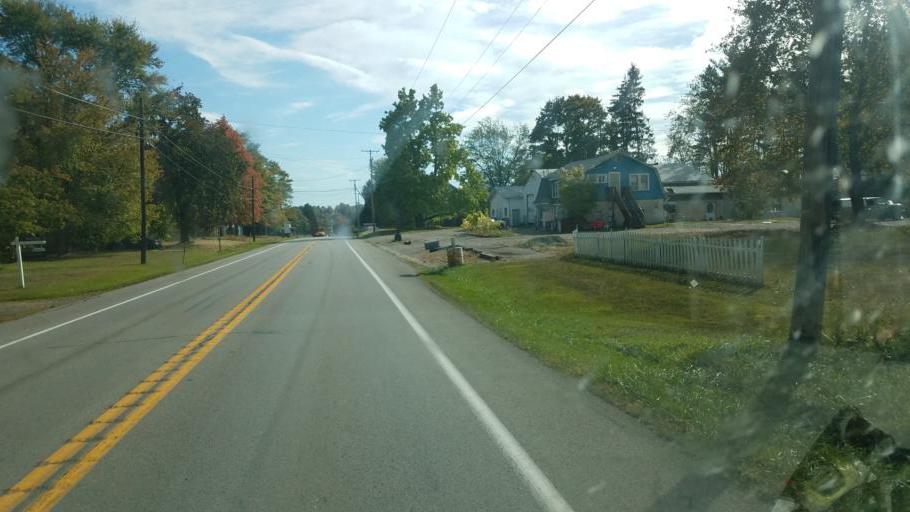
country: US
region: Pennsylvania
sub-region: Mercer County
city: Mercer
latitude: 41.2444
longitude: -80.2383
